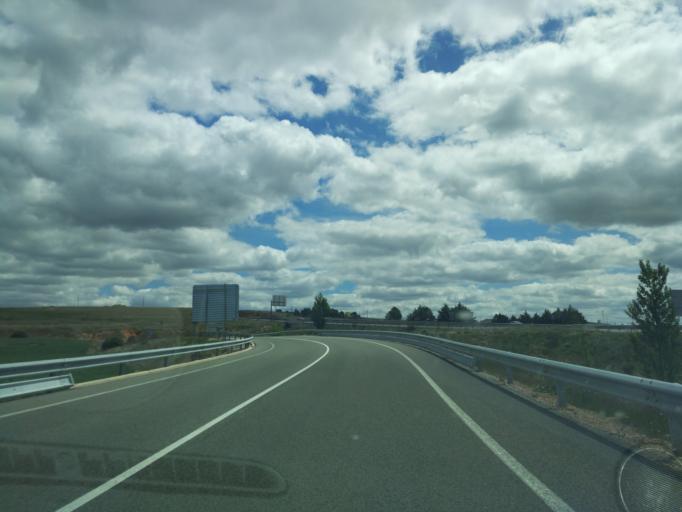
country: ES
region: Castille-La Mancha
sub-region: Provincia de Guadalajara
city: Torremocha del Campo
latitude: 40.9864
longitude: -2.6099
